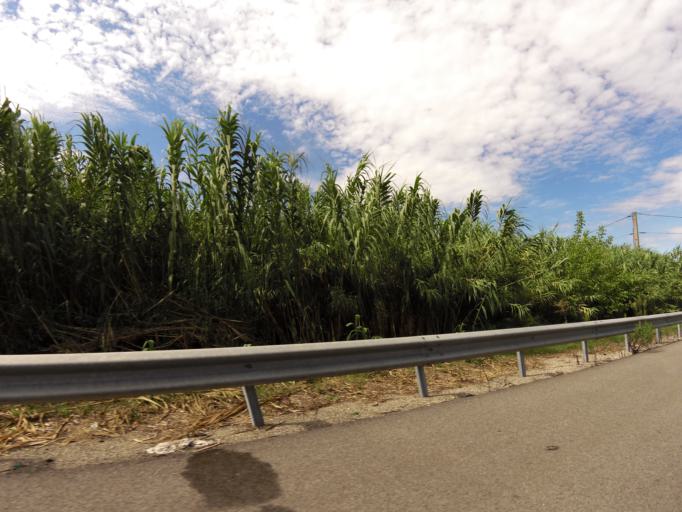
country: FR
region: Languedoc-Roussillon
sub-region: Departement de l'Herault
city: Marsillargues
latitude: 43.6381
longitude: 4.1925
